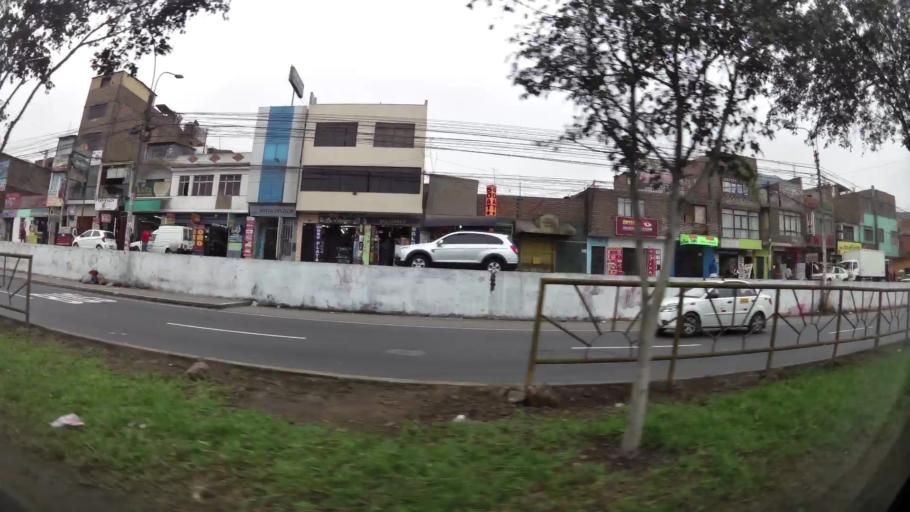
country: PE
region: Lima
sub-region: Lima
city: Independencia
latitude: -11.9564
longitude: -77.0526
